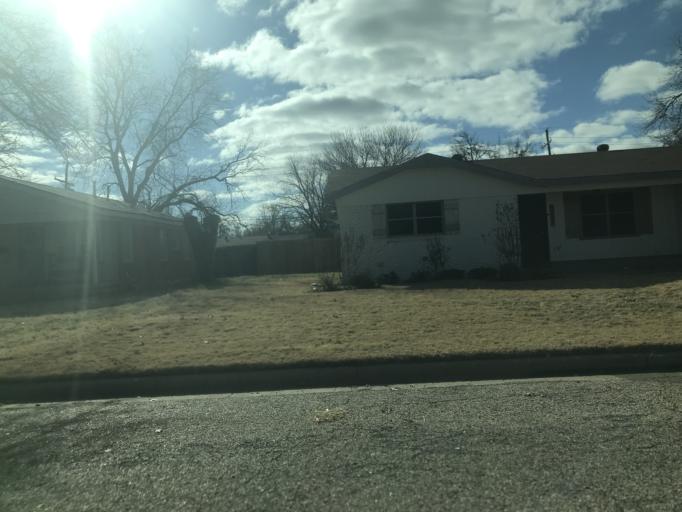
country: US
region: Texas
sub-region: Taylor County
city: Abilene
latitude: 32.4637
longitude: -99.7711
